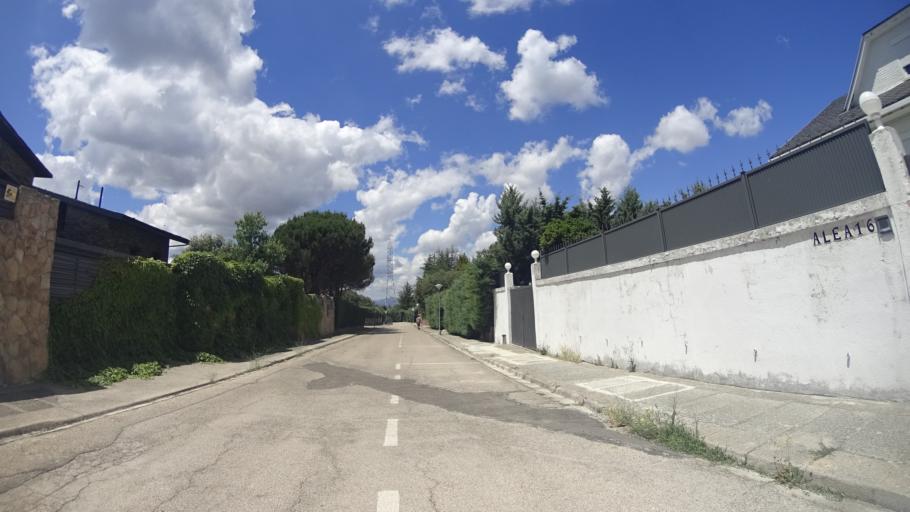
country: ES
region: Madrid
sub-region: Provincia de Madrid
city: Hoyo de Manzanares
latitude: 40.6131
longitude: -3.9321
